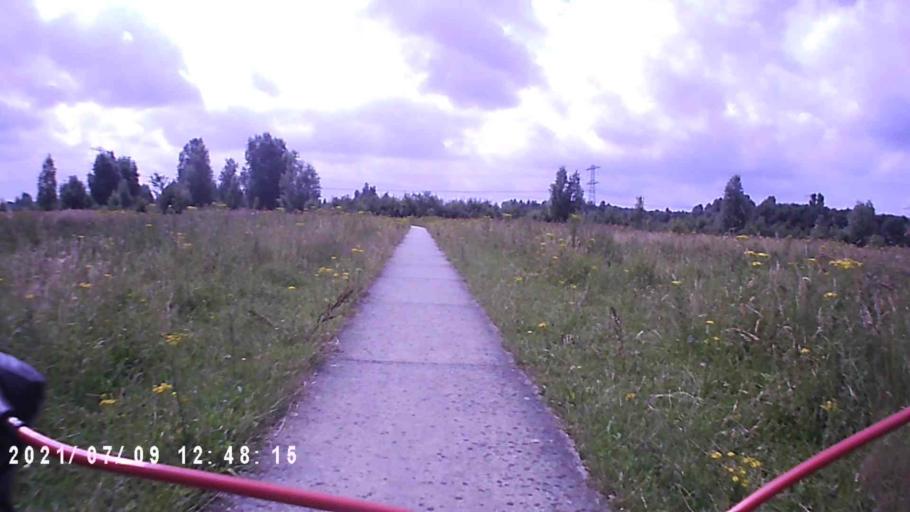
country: NL
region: Groningen
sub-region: Gemeente  Oldambt
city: Winschoten
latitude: 53.1260
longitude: 7.0351
